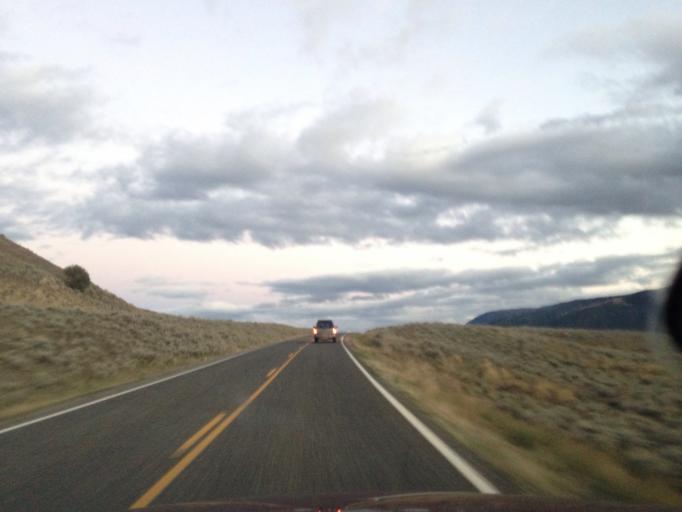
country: US
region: Montana
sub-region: Park County
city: Livingston
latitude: 44.8888
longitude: -110.2254
